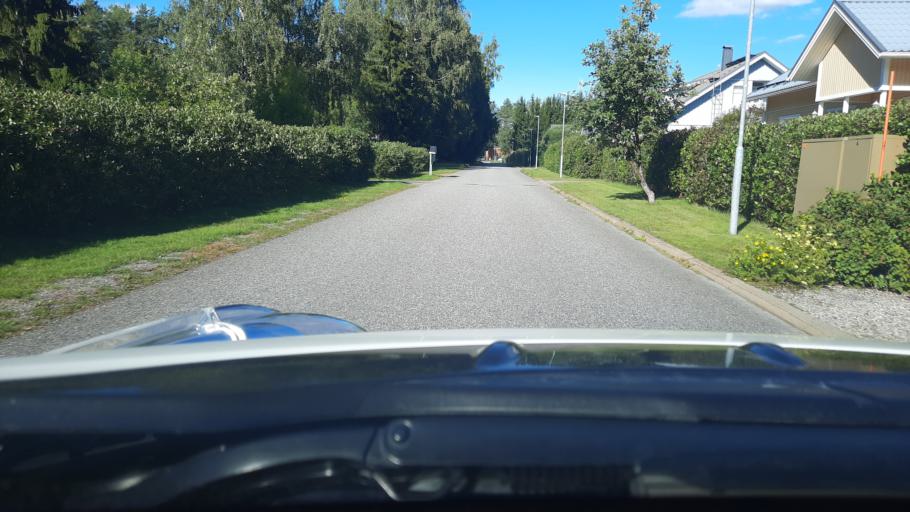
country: FI
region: North Karelia
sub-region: Joensuu
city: Joensuu
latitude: 62.6359
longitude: 29.6845
